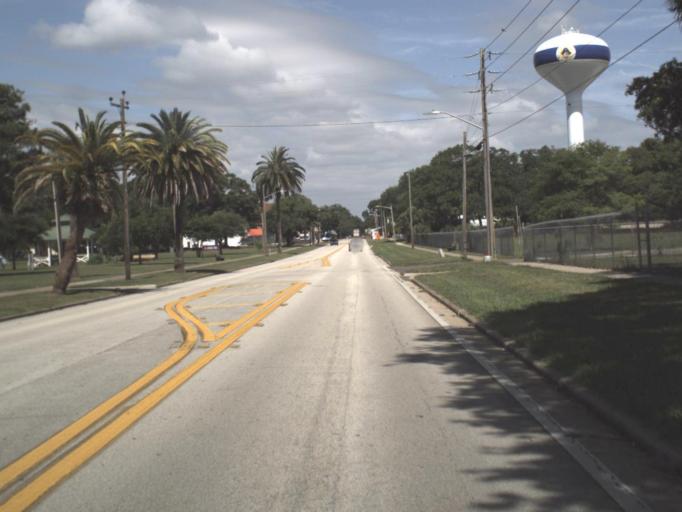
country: US
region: Florida
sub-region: Nassau County
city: Fernandina Beach
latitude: 30.6702
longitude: -81.4535
